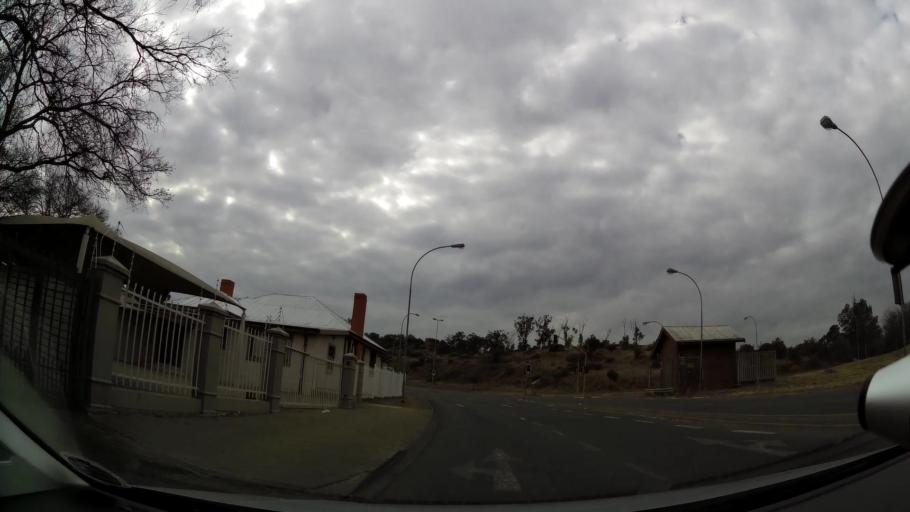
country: ZA
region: Orange Free State
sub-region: Mangaung Metropolitan Municipality
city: Bloemfontein
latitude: -29.1052
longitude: 26.2136
